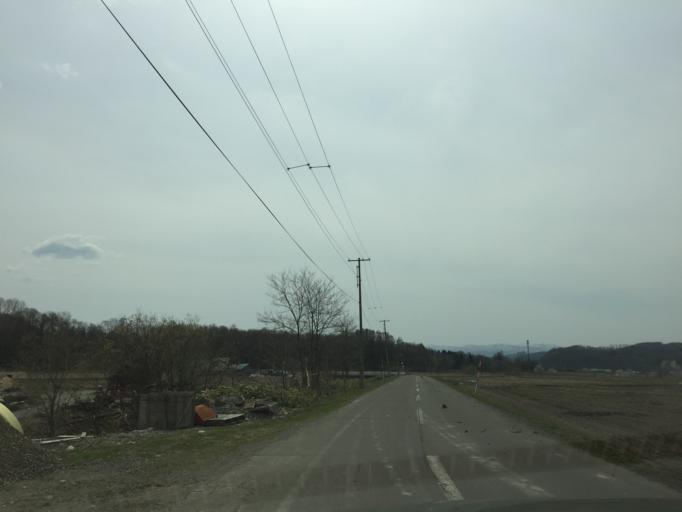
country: JP
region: Hokkaido
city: Ashibetsu
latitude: 43.6160
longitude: 142.2156
